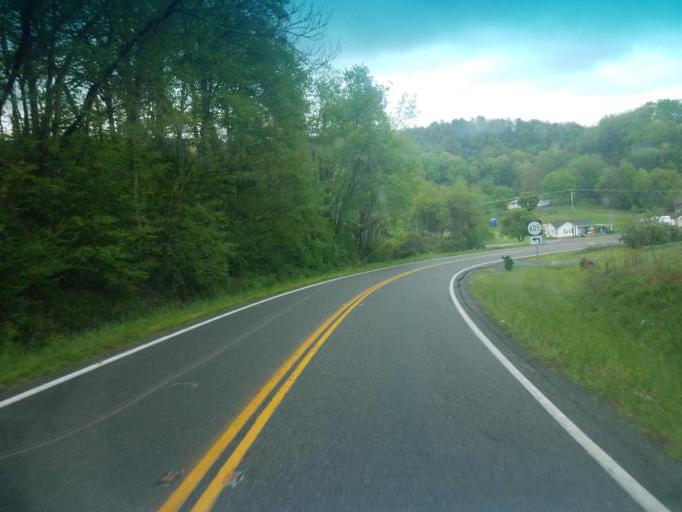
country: US
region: Virginia
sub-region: Washington County
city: Emory
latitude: 36.6484
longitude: -81.7847
